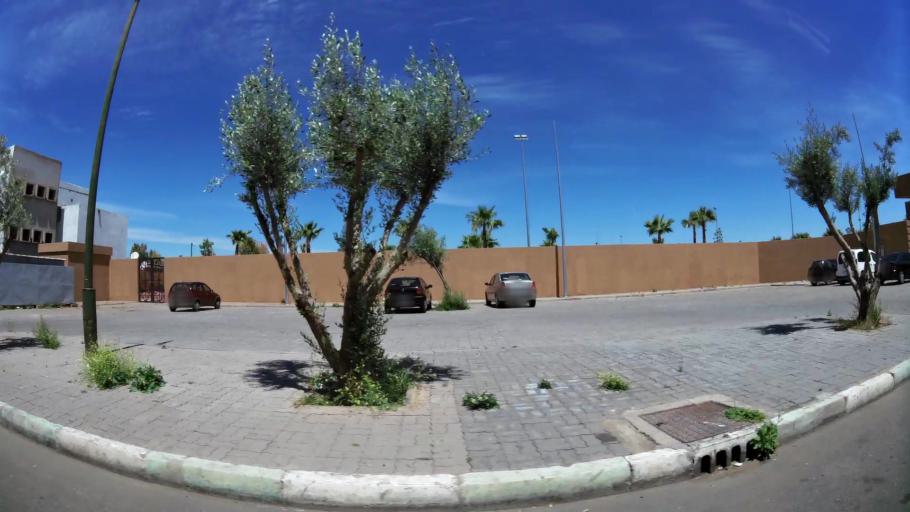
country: MA
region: Marrakech-Tensift-Al Haouz
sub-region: Marrakech
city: Marrakesh
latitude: 31.6312
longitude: -8.0447
